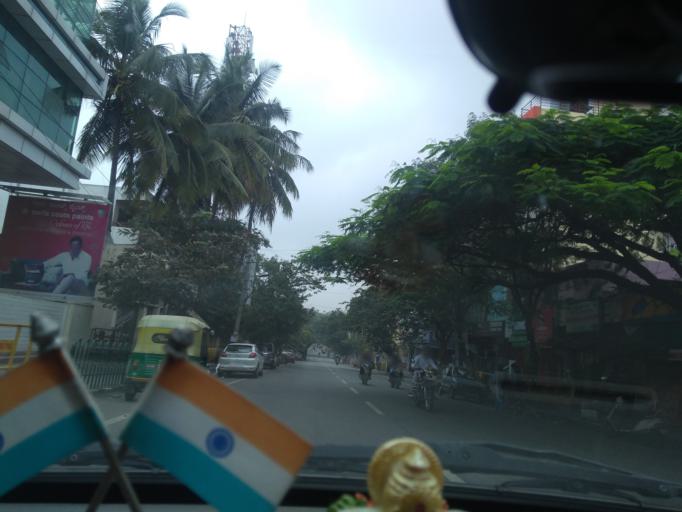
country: IN
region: Karnataka
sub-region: Bangalore Urban
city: Bangalore
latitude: 13.0017
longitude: 77.5503
